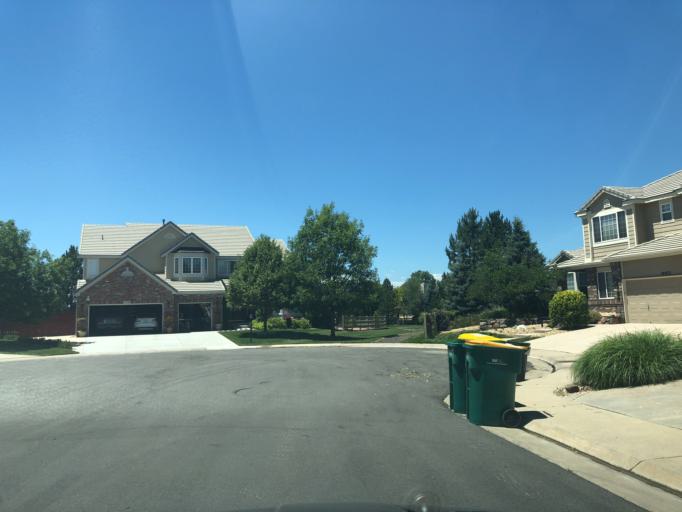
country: US
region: Colorado
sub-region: Arapahoe County
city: Dove Valley
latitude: 39.6080
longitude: -104.7602
